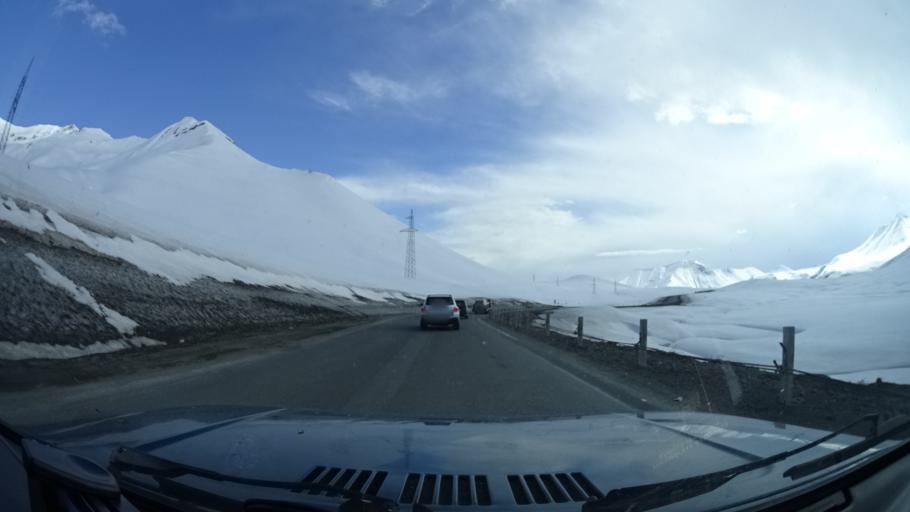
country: GE
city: Gudauri
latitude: 42.5118
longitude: 44.4623
